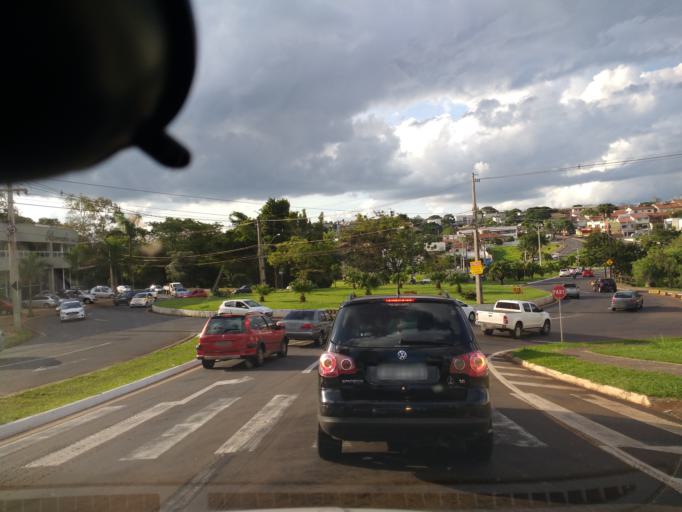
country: BR
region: Parana
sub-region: Londrina
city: Londrina
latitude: -23.3265
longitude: -51.1772
